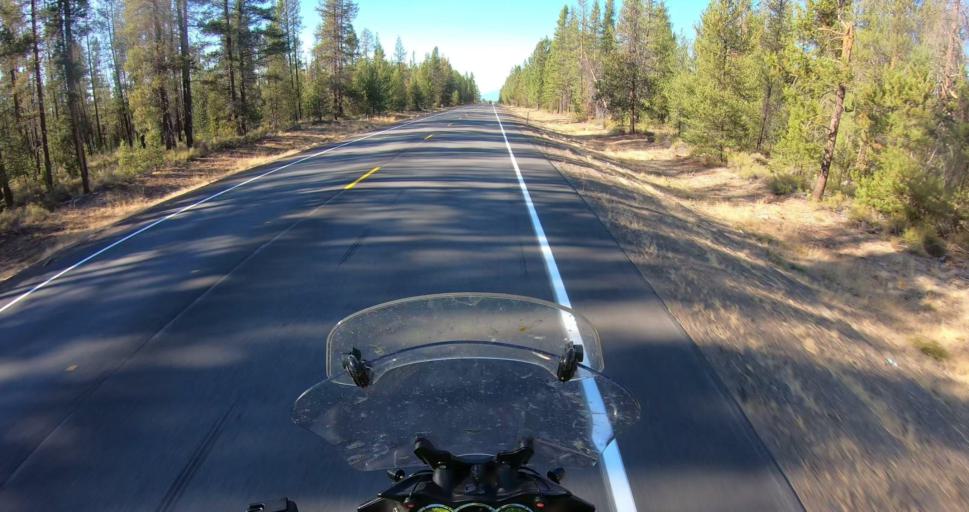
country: US
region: Oregon
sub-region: Deschutes County
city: La Pine
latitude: 43.5556
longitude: -121.4741
